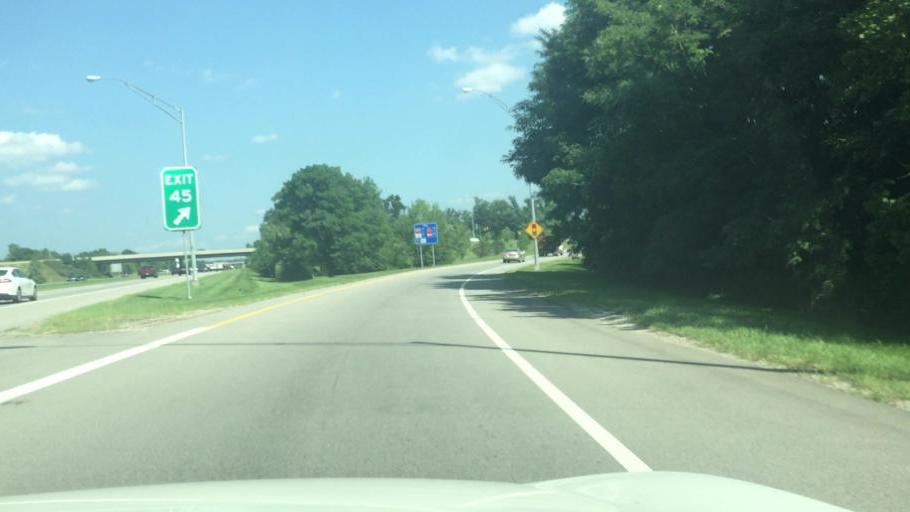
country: US
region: Ohio
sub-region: Franklin County
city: New Albany
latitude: 40.0914
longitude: -82.8272
